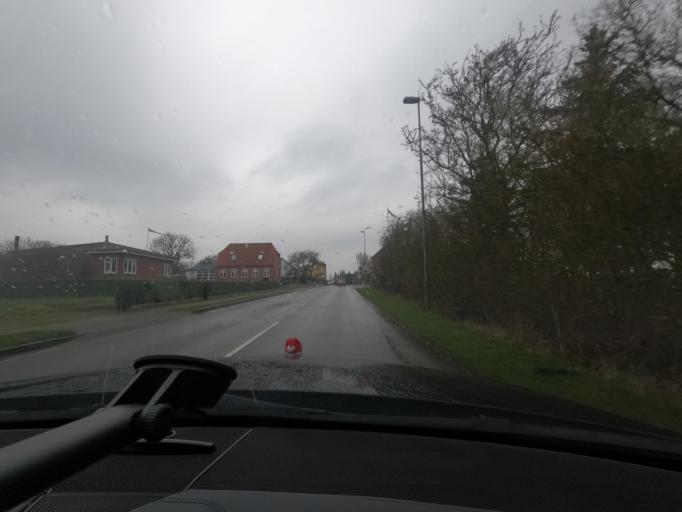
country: DK
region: South Denmark
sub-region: Sonderborg Kommune
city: Horuphav
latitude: 54.8804
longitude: 9.9950
